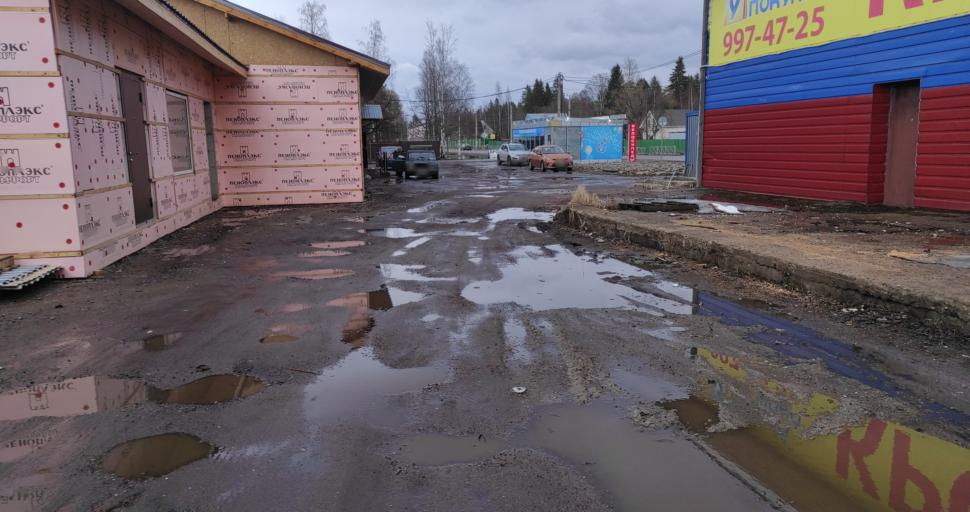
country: RU
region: Leningrad
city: Roshchino
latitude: 60.2532
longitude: 29.5761
